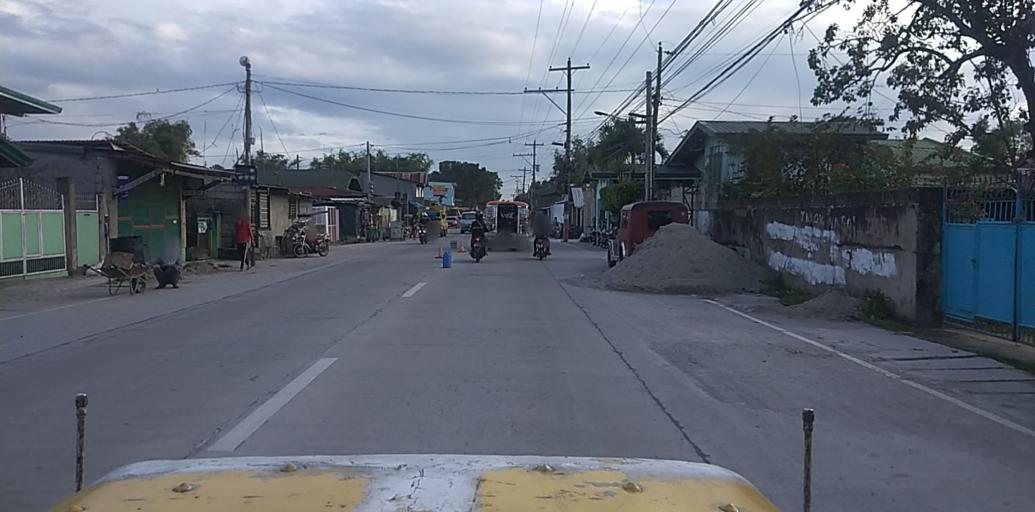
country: PH
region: Central Luzon
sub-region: Province of Pampanga
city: Anao
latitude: 15.1429
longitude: 120.6924
